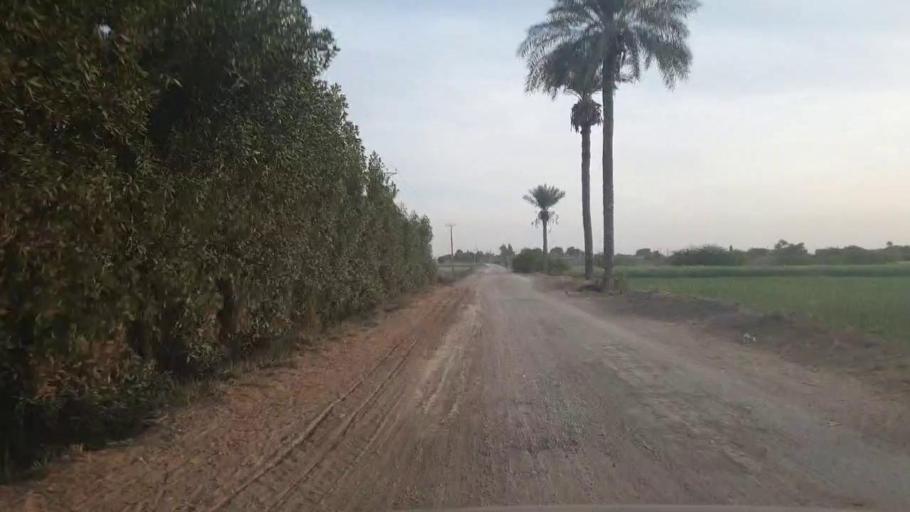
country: PK
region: Sindh
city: Kunri
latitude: 25.2237
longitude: 69.5740
